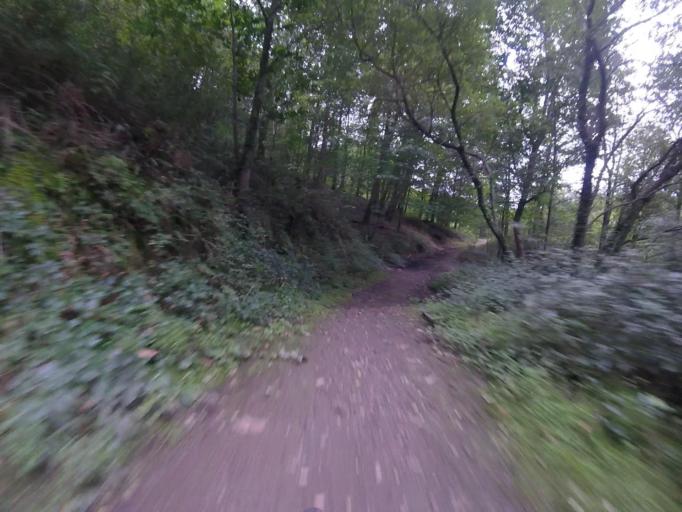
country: ES
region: Basque Country
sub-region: Provincia de Guipuzcoa
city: Errenteria
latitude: 43.2725
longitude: -1.8381
